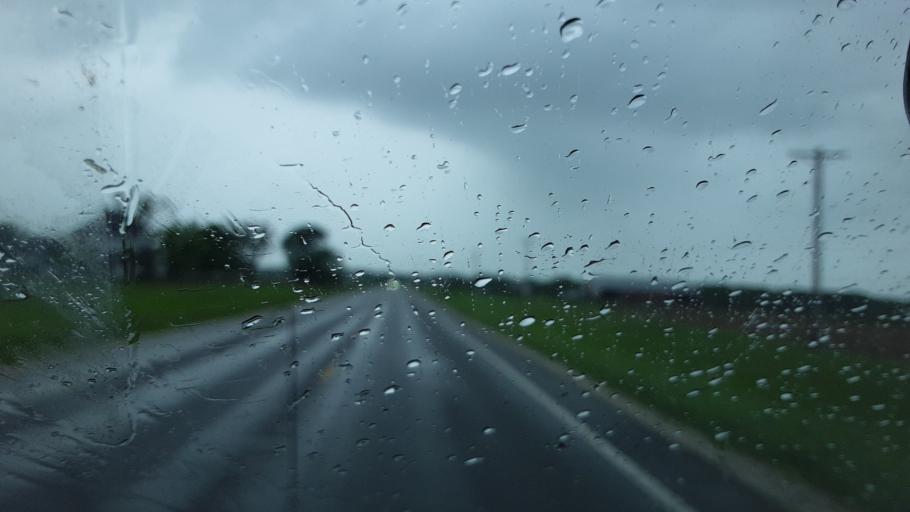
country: US
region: Missouri
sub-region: Monroe County
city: Paris
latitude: 39.4770
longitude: -92.1894
